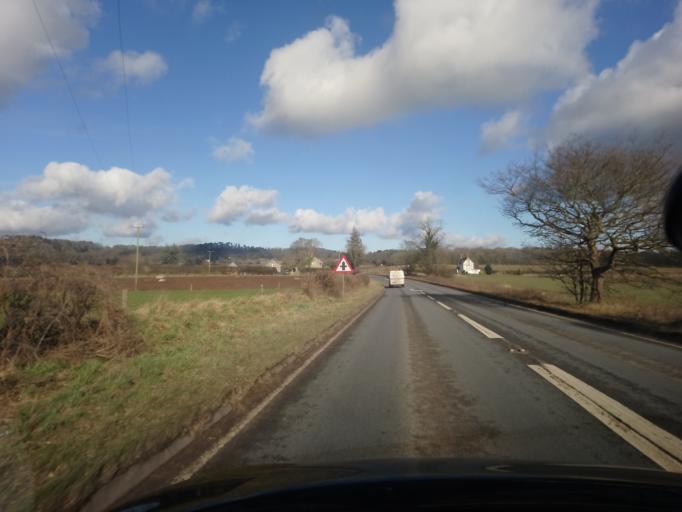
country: GB
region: England
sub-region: Shropshire
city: Clive
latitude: 52.7932
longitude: -2.7021
